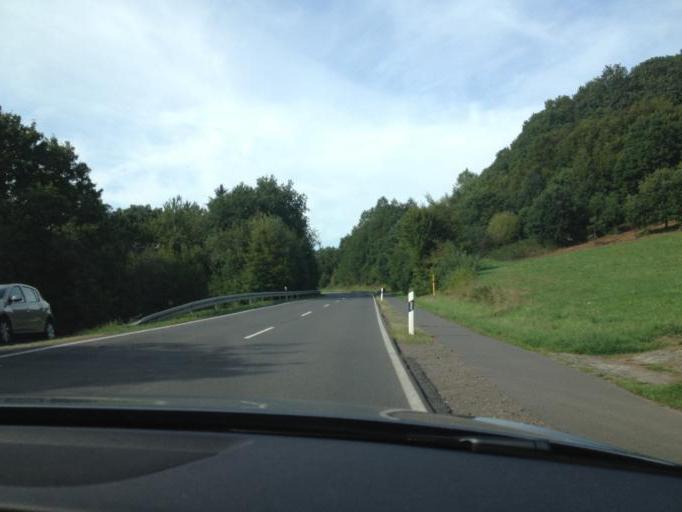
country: DE
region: Rheinland-Pfalz
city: Breitenbach
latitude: 49.4232
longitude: 7.2656
